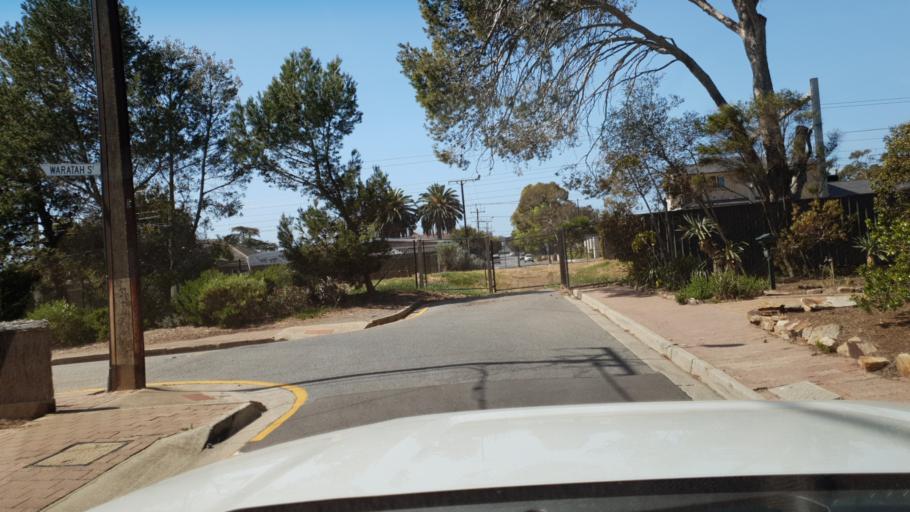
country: AU
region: South Australia
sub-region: Adelaide Hills
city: Seacliff
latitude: -35.0363
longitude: 138.5205
